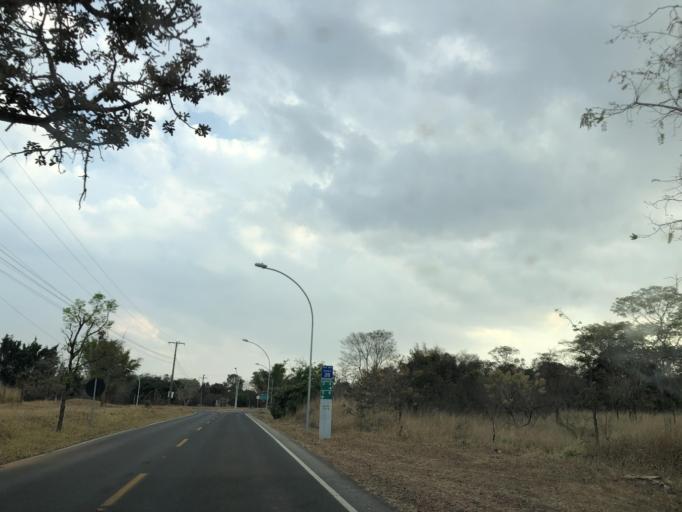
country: BR
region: Federal District
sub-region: Brasilia
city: Brasilia
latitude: -15.9374
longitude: -47.9747
